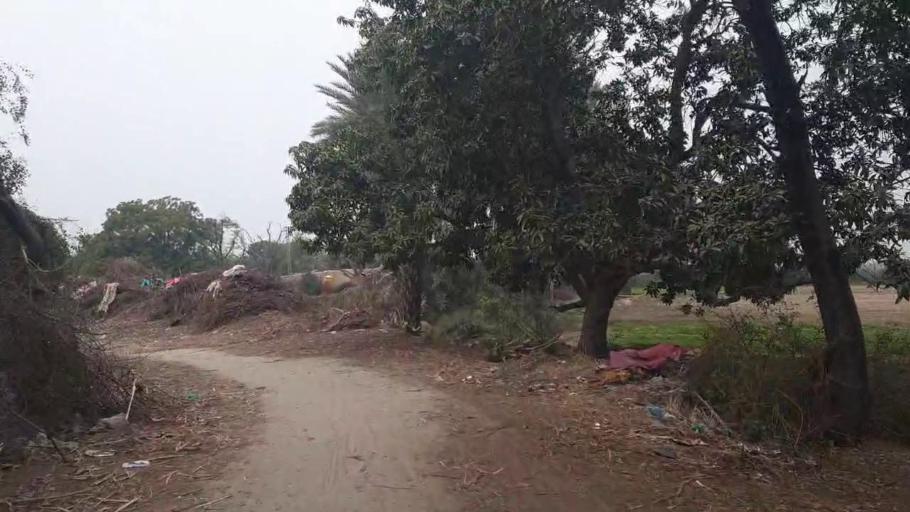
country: PK
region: Sindh
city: Shahdadpur
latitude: 25.8628
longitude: 68.6474
